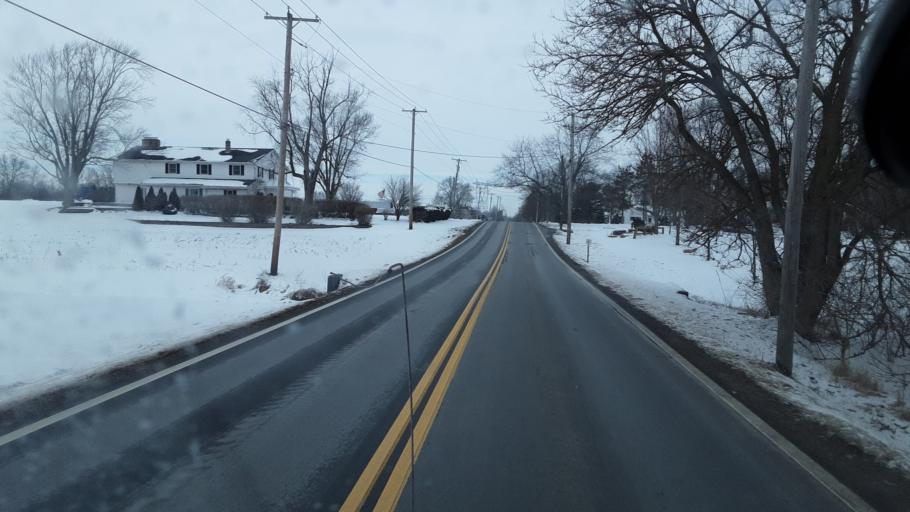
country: US
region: Ohio
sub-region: Delaware County
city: Powell
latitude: 40.2245
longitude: -83.1502
